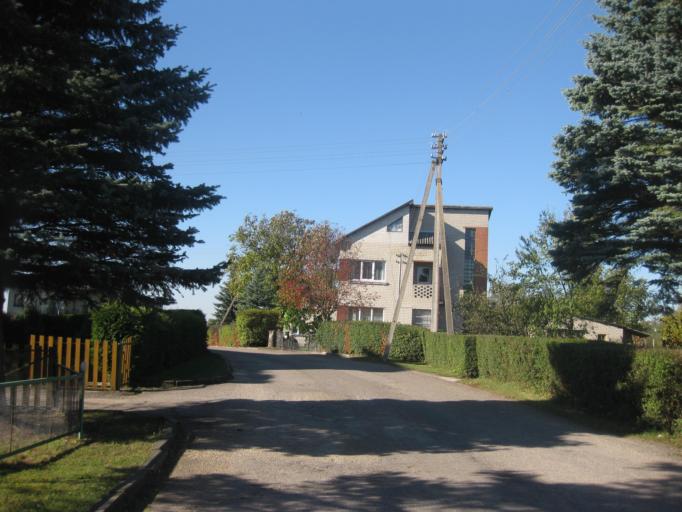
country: LT
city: Vilkija
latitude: 55.0444
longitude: 23.5743
